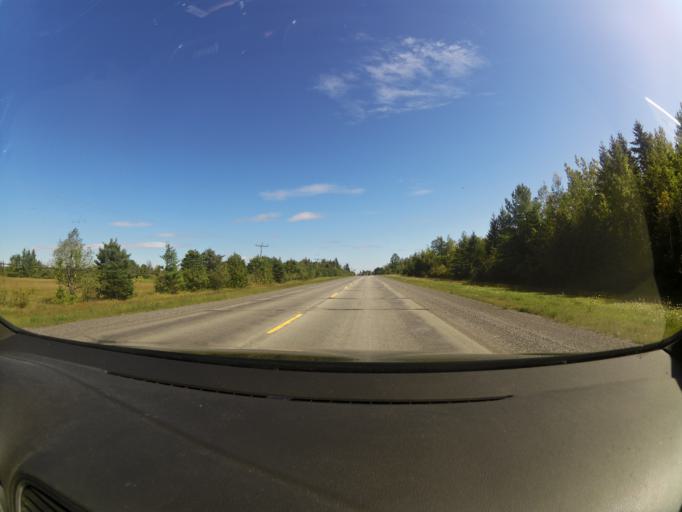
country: CA
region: Ontario
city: Bells Corners
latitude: 45.2592
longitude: -75.9497
